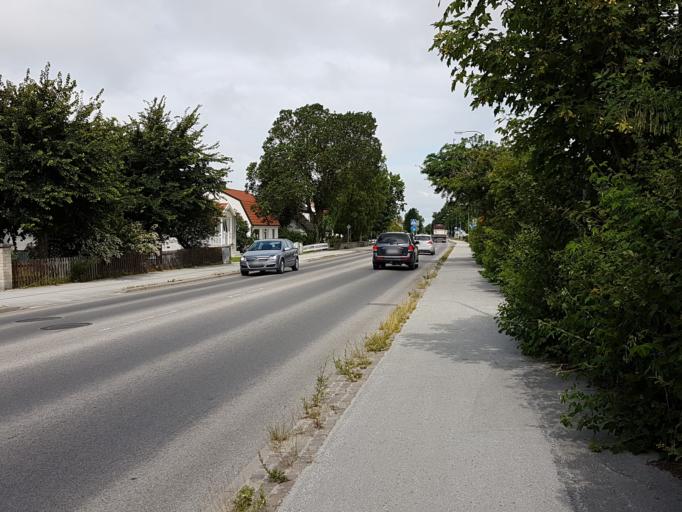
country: SE
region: Gotland
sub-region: Gotland
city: Visby
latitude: 57.6297
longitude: 18.3154
